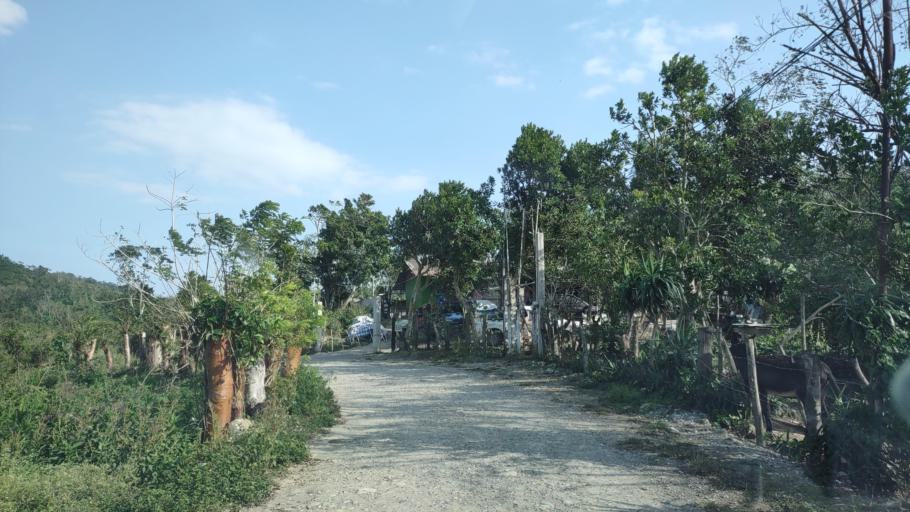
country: MX
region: Veracruz
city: Papantla de Olarte
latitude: 20.4581
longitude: -97.3932
